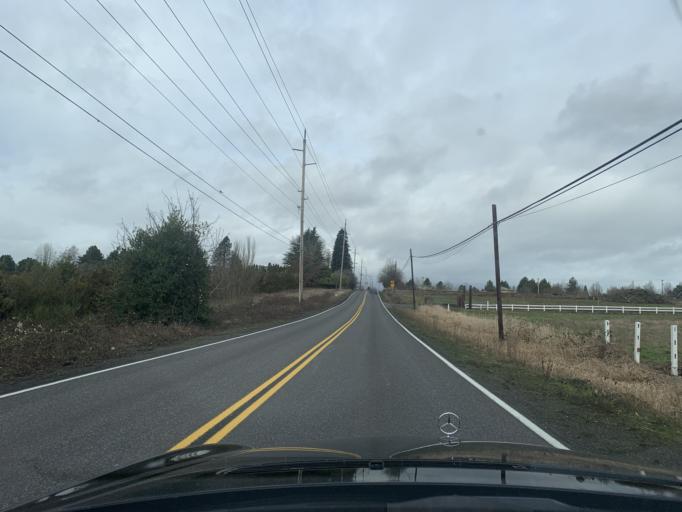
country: US
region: Oregon
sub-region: Multnomah County
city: Gresham
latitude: 45.4695
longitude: -122.4669
